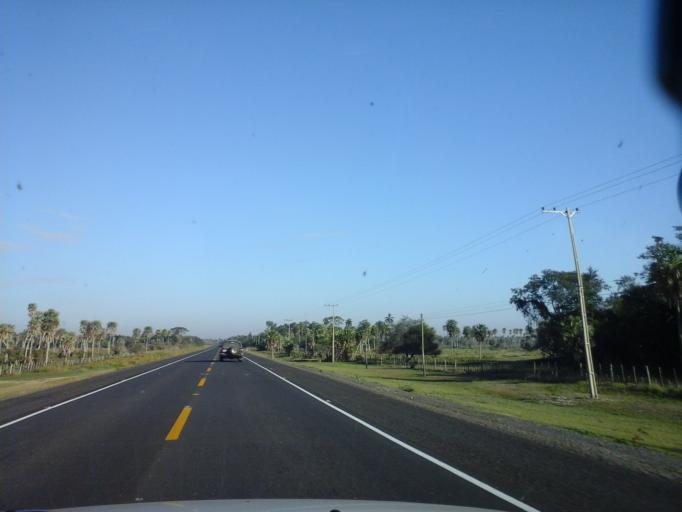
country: PY
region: Neembucu
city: Pilar
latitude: -26.8535
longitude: -58.0461
